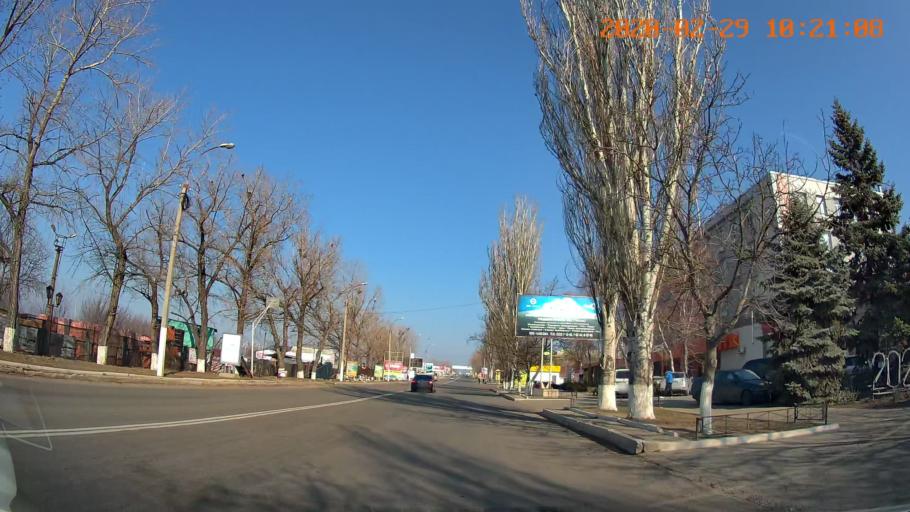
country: MD
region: Telenesti
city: Tiraspolul Nou
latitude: 46.8640
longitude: 29.6098
